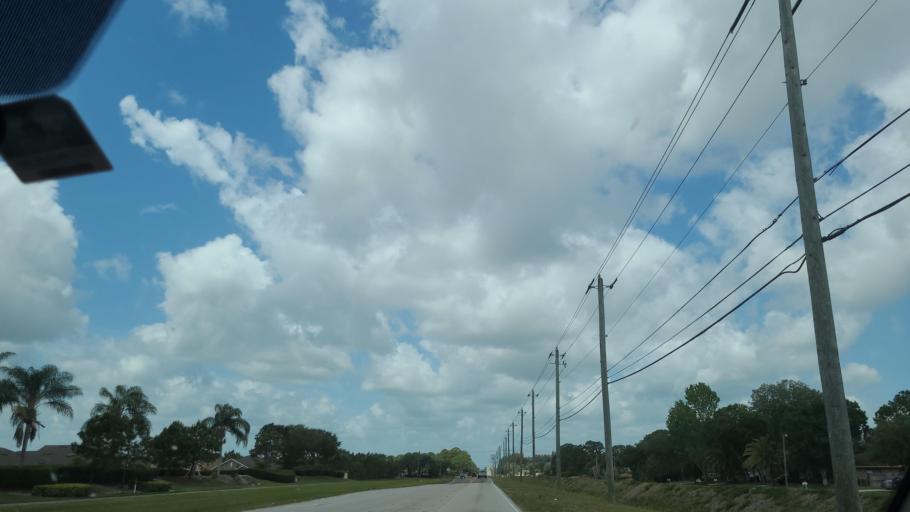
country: US
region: Florida
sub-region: Brevard County
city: June Park
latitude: 27.9991
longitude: -80.6827
